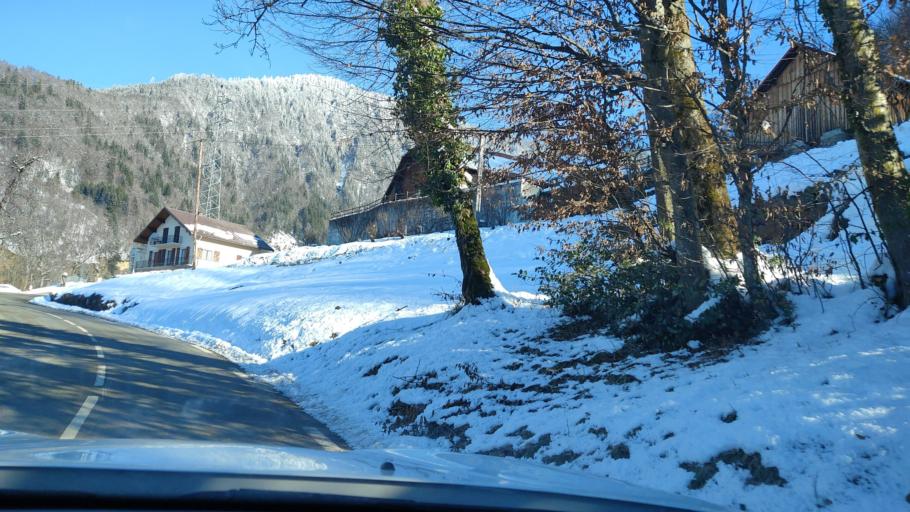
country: FR
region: Rhone-Alpes
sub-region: Departement de la Savoie
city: Ugine
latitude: 45.7562
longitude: 6.4443
